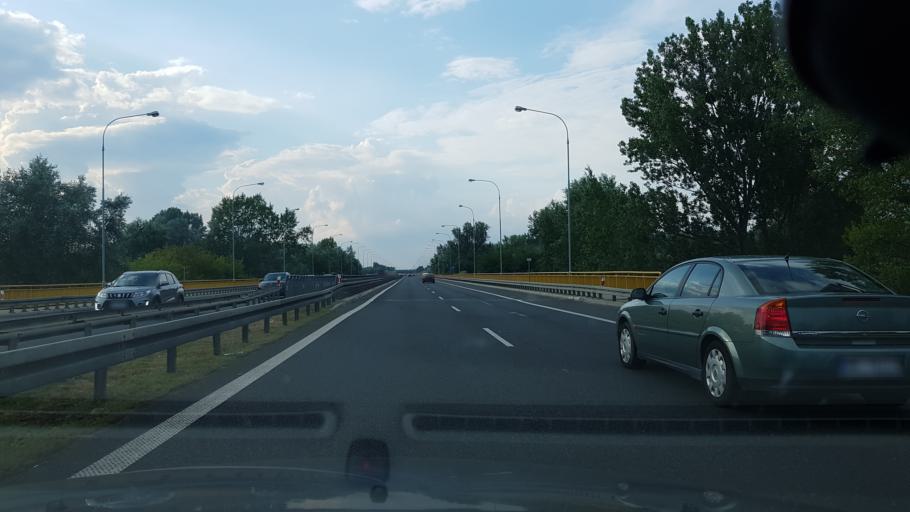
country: PL
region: Masovian Voivodeship
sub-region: Powiat nowodworski
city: Zakroczym
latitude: 52.4233
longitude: 20.6591
